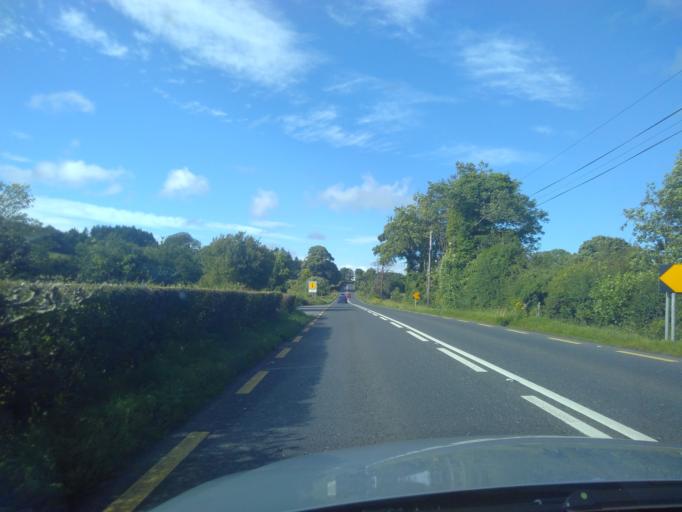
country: IE
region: Ulster
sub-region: County Donegal
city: Ballybofey
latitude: 54.8165
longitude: -7.7578
